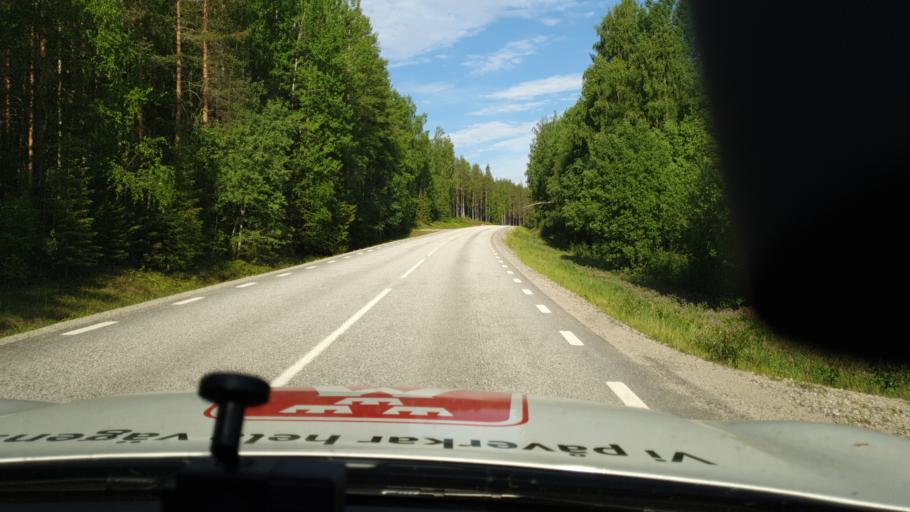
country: SE
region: Vaesterbotten
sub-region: Vindelns Kommun
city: Vindeln
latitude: 64.2094
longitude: 19.5078
